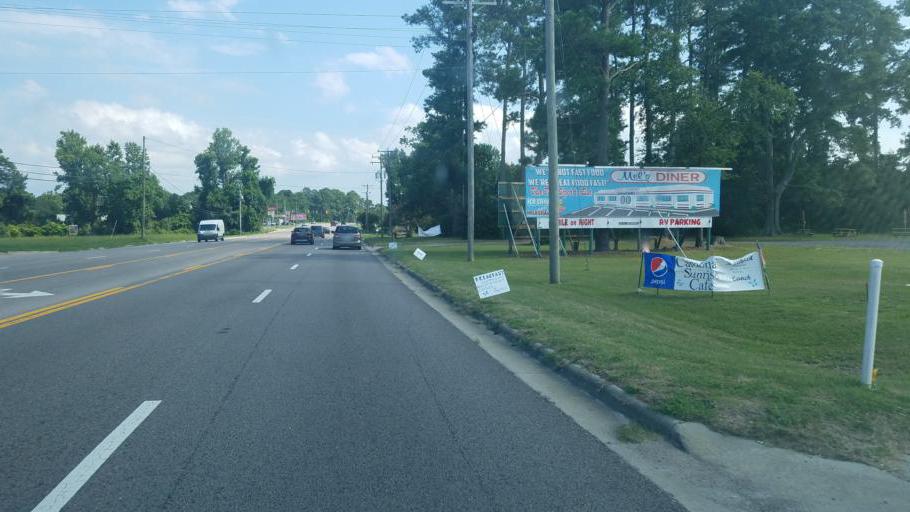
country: US
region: North Carolina
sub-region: Dare County
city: Southern Shores
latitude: 36.2421
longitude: -75.8779
